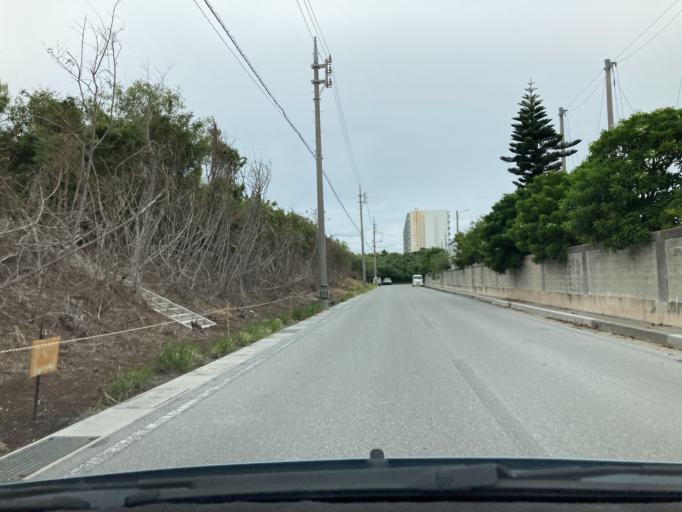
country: JP
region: Okinawa
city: Itoman
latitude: 26.1288
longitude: 127.6537
